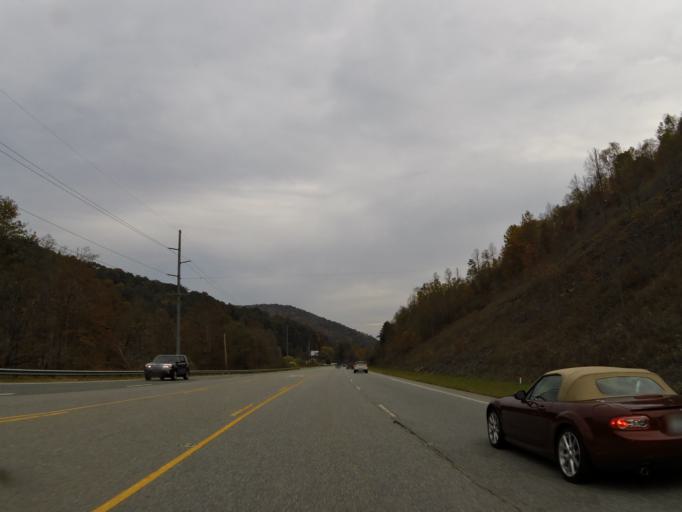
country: US
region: North Carolina
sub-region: Caldwell County
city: Lenoir
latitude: 36.0252
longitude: -81.5786
